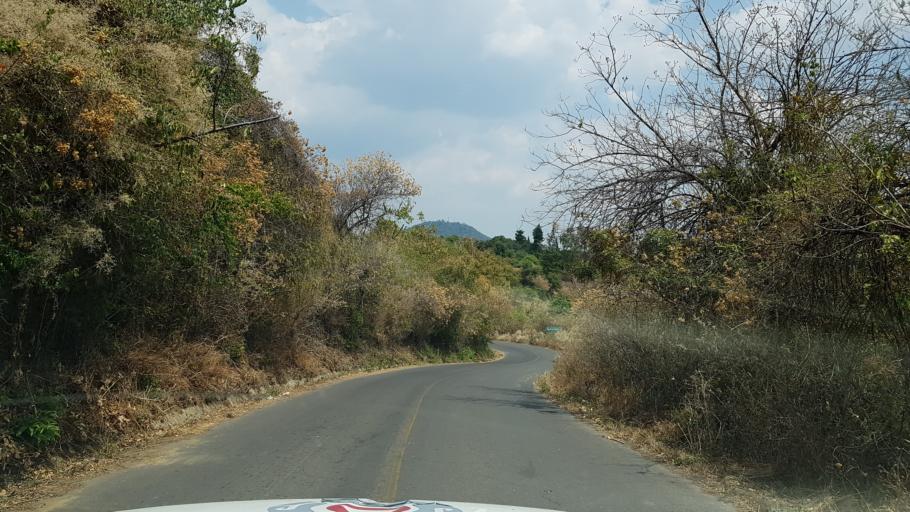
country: MX
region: Morelos
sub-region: Yecapixtla
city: Texcala
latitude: 18.9196
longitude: -98.8115
